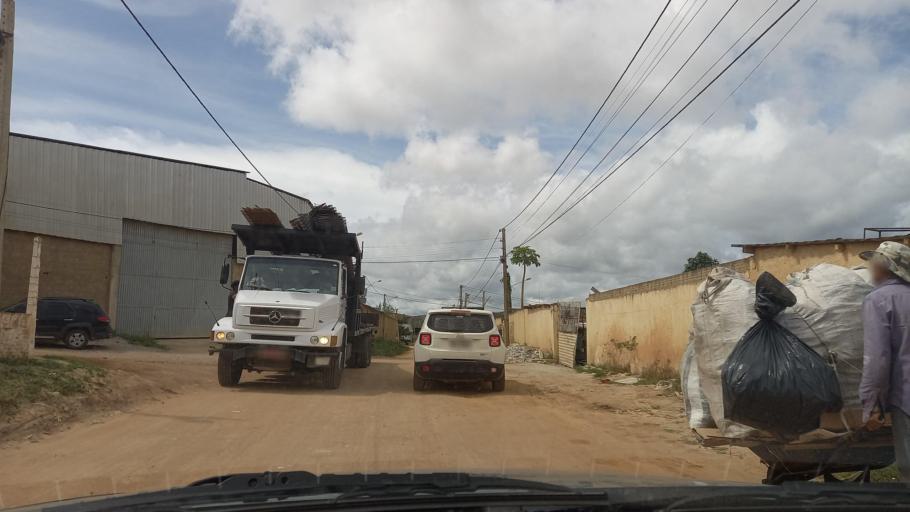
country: BR
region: Pernambuco
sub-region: Gravata
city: Gravata
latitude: -8.1864
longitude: -35.5819
